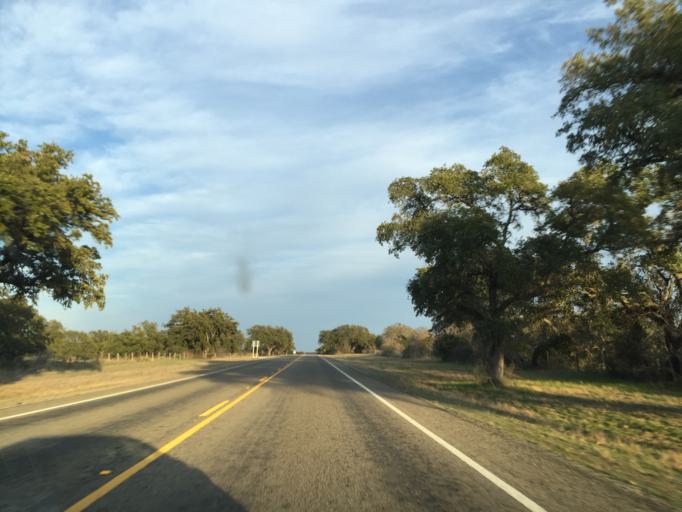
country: US
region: Texas
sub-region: Llano County
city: Buchanan Dam
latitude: 30.7329
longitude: -98.4818
